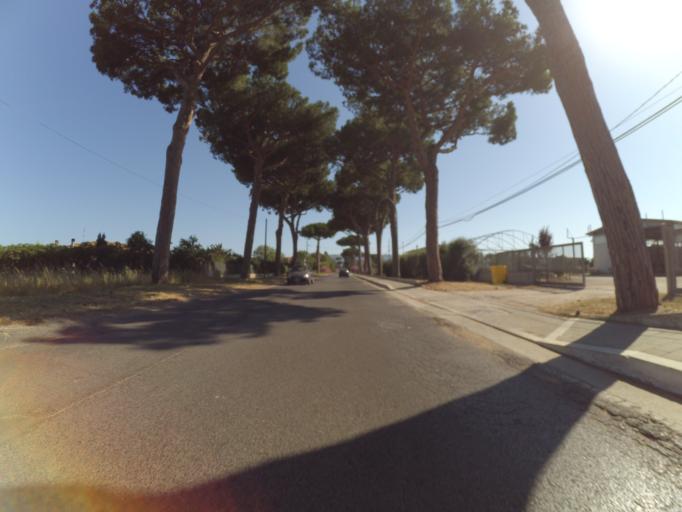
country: IT
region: Latium
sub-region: Provincia di Latina
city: San Felice Circeo
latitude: 41.2841
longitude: 13.1050
